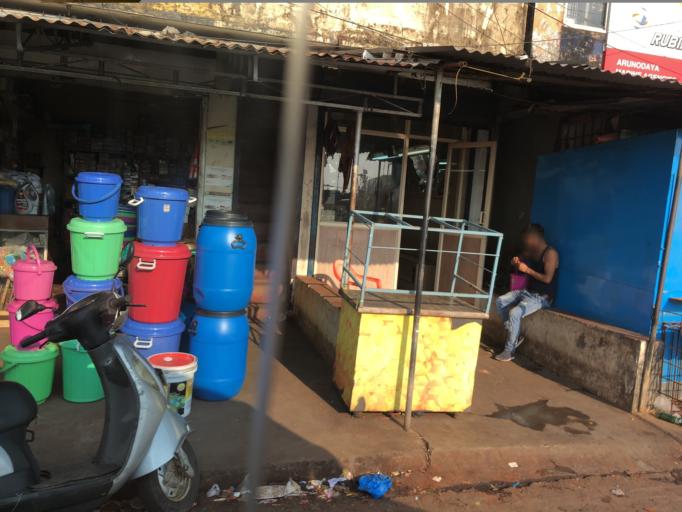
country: IN
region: Karnataka
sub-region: Dakshina Kannada
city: Ullal
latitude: 12.8578
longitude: 74.8327
